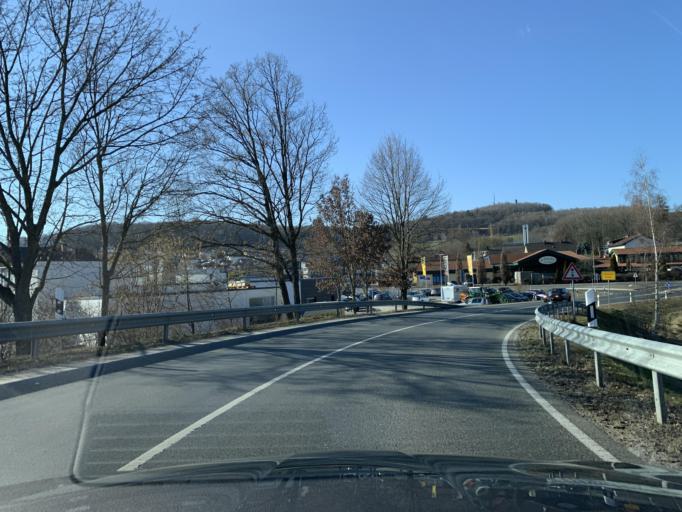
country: DE
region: Bavaria
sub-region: Upper Palatinate
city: Cham
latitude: 49.2271
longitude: 12.6749
